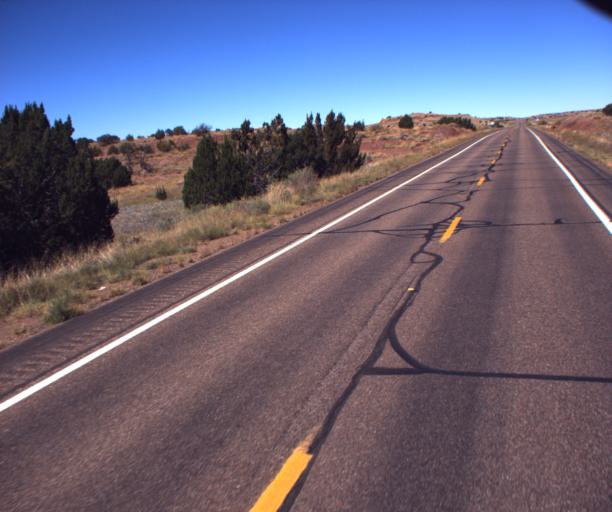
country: US
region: Arizona
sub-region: Apache County
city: Saint Johns
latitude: 34.3881
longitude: -109.4068
